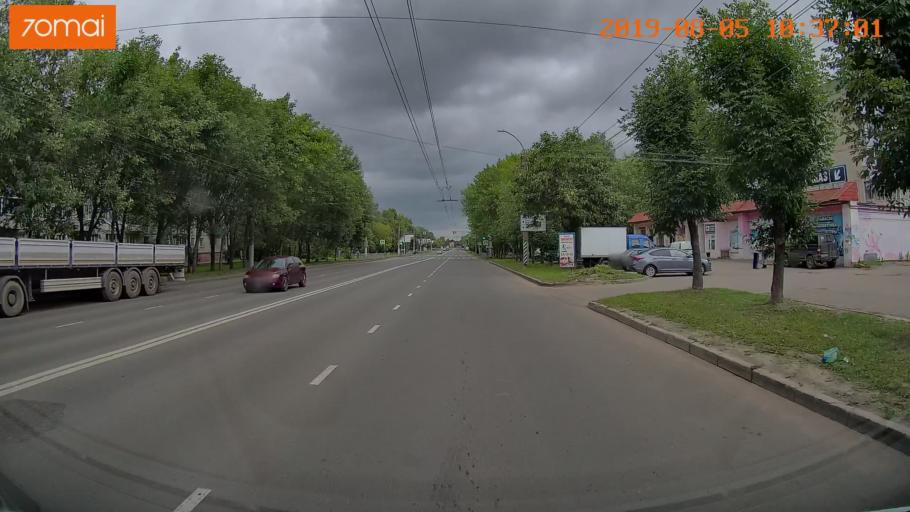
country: RU
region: Ivanovo
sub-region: Gorod Ivanovo
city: Ivanovo
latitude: 56.9661
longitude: 41.0057
